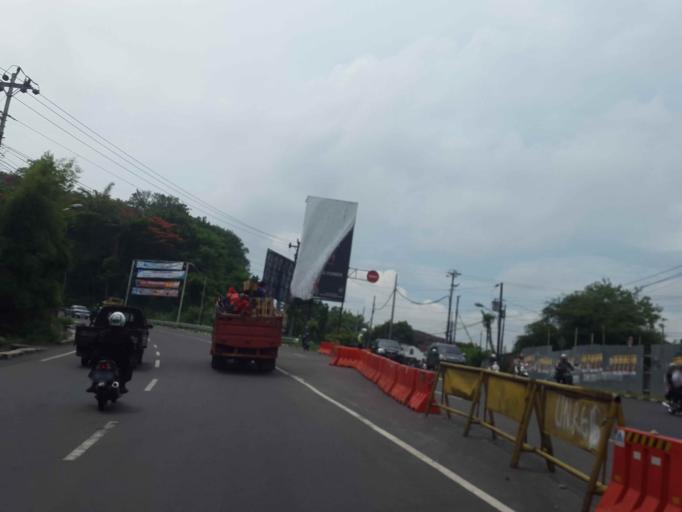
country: ID
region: Central Java
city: Semarang
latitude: -7.0340
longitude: 110.4176
